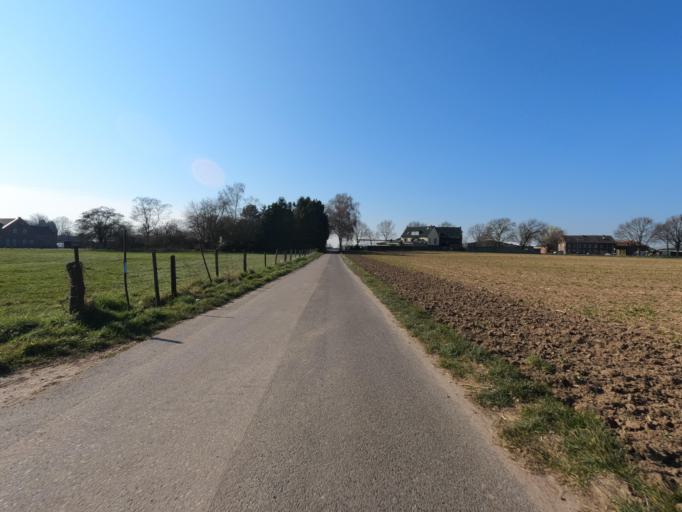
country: DE
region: North Rhine-Westphalia
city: Erkelenz
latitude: 51.0601
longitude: 6.2978
